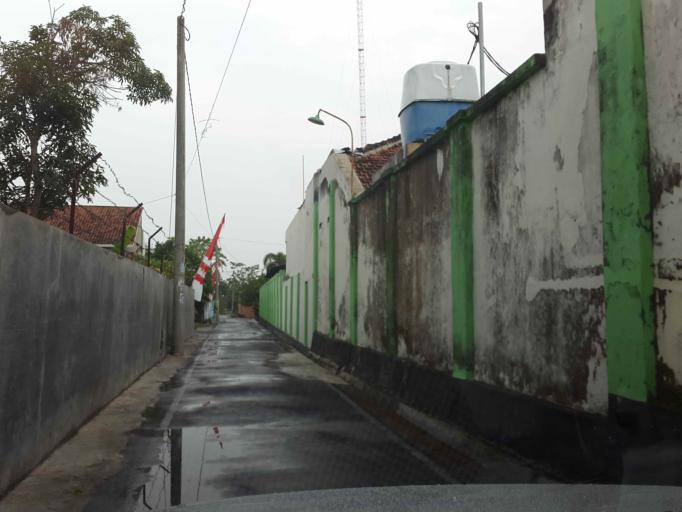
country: ID
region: Central Java
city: Jaten
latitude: -7.5999
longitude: 110.9622
